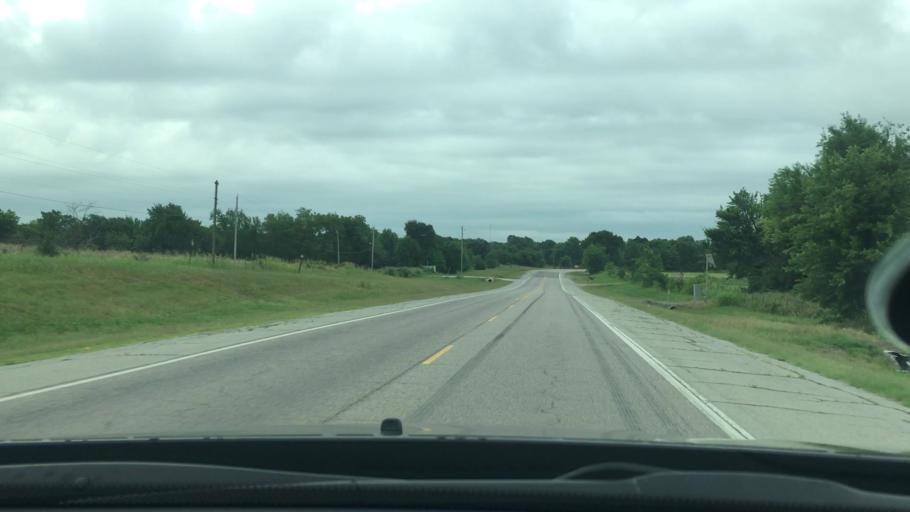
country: US
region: Oklahoma
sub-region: Coal County
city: Coalgate
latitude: 34.5506
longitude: -96.2340
